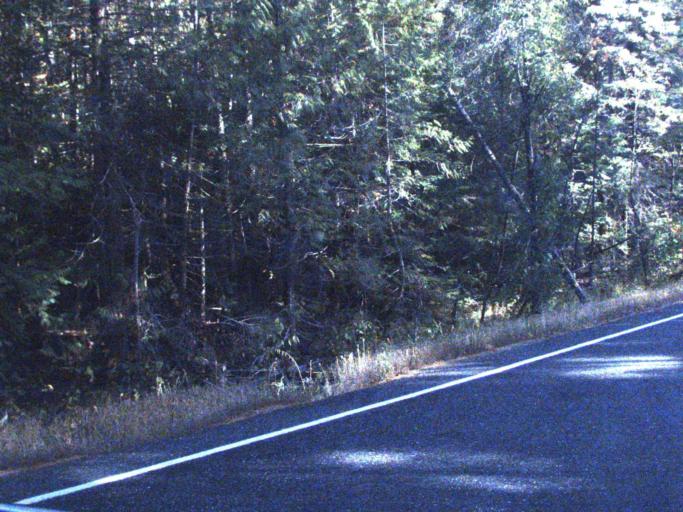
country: US
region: Washington
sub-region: Stevens County
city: Kettle Falls
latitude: 48.5946
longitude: -118.3336
